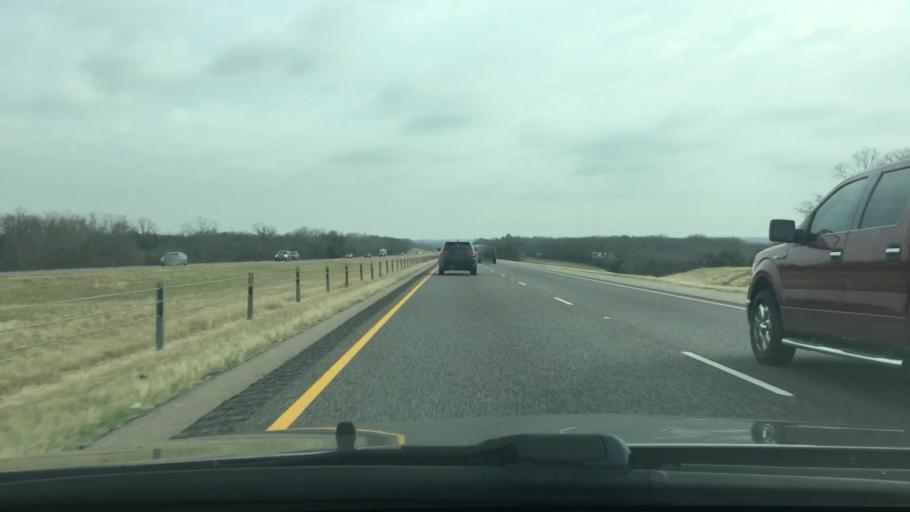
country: US
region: Texas
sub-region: Leon County
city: Buffalo
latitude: 31.5266
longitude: -96.1139
